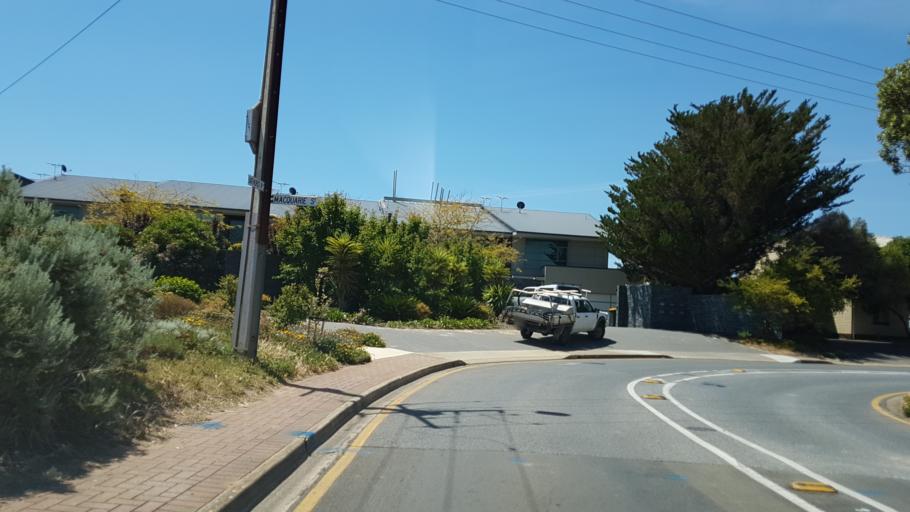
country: AU
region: South Australia
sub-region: Onkaparinga
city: Moana
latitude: -35.2064
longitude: 138.4732
